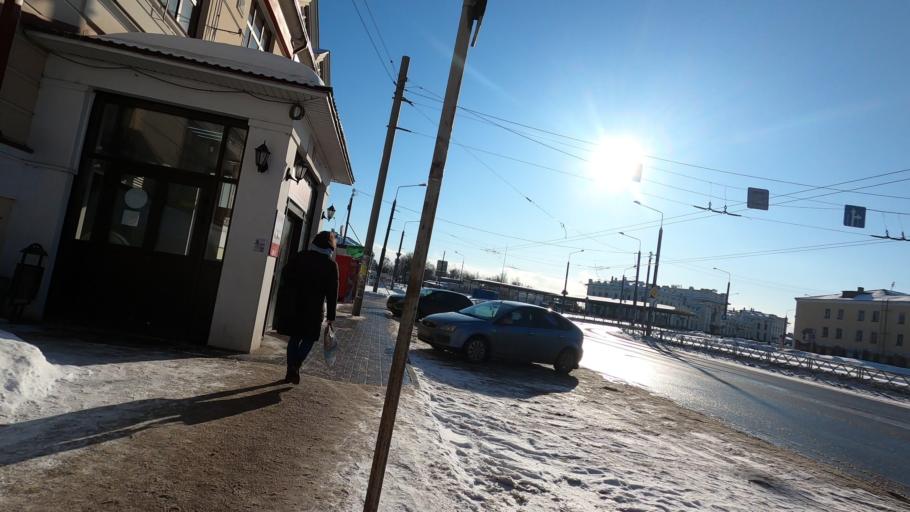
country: RU
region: Jaroslavl
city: Rybinsk
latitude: 58.0430
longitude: 38.8366
